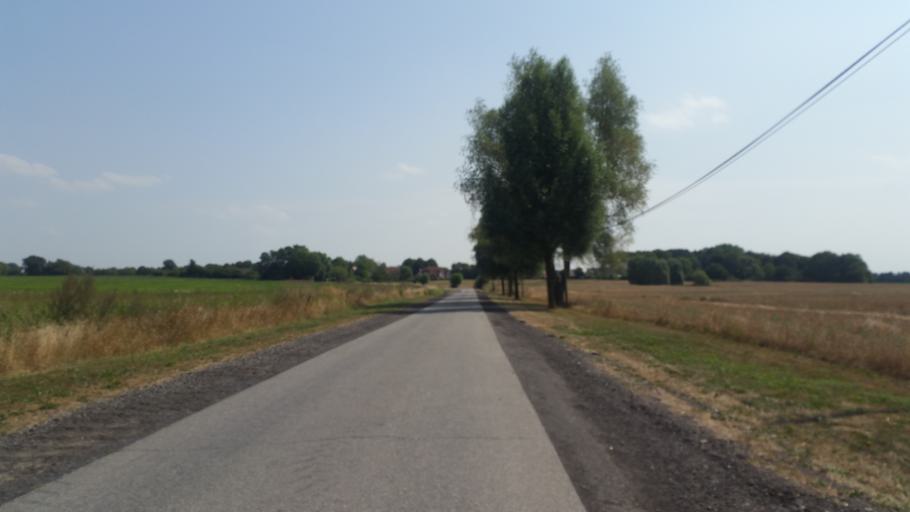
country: DE
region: Mecklenburg-Vorpommern
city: Bastorf
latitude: 54.0959
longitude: 11.6372
